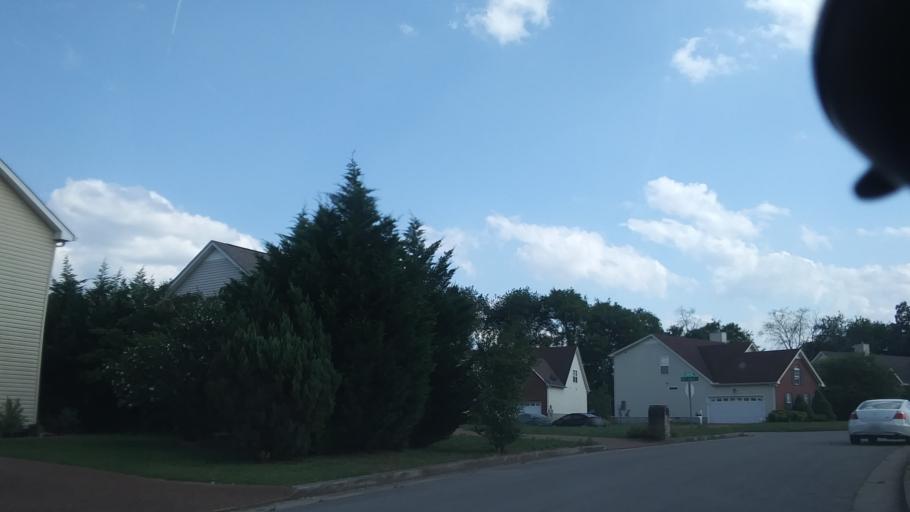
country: US
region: Tennessee
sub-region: Rutherford County
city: La Vergne
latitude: 36.0891
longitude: -86.6545
